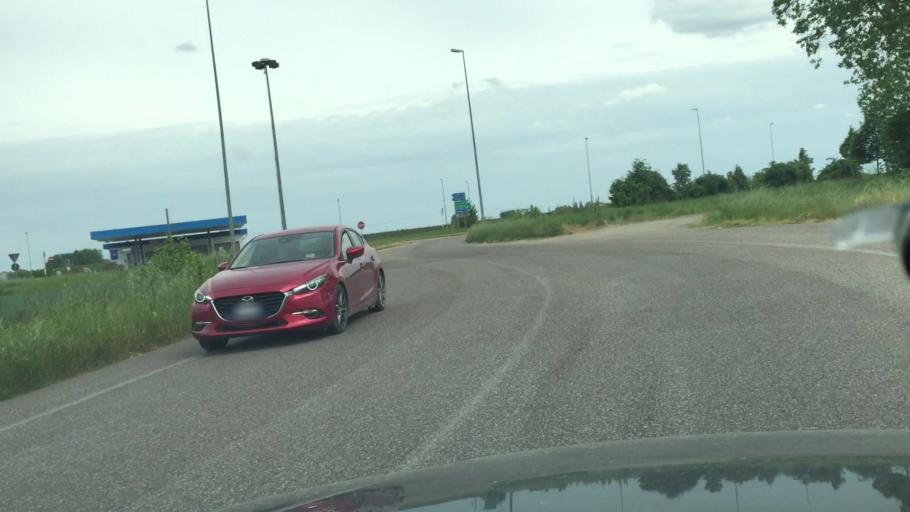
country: IT
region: Emilia-Romagna
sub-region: Provincia di Ferrara
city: Cona
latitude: 44.7983
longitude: 11.7213
